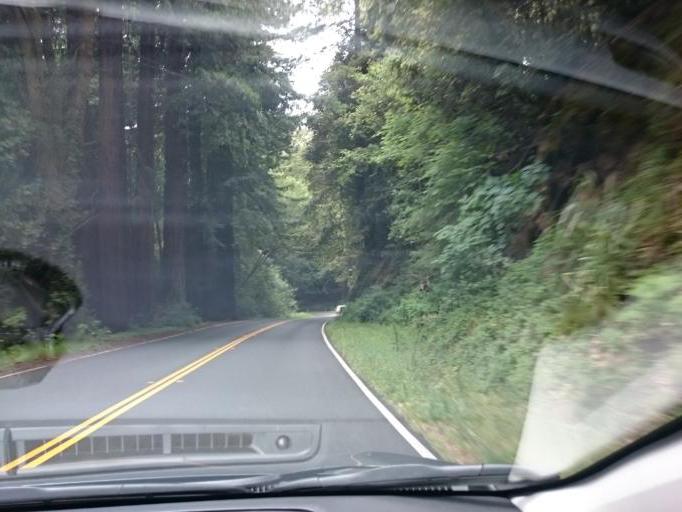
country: US
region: California
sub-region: Mendocino County
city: Fort Bragg
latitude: 39.1800
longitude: -123.6962
